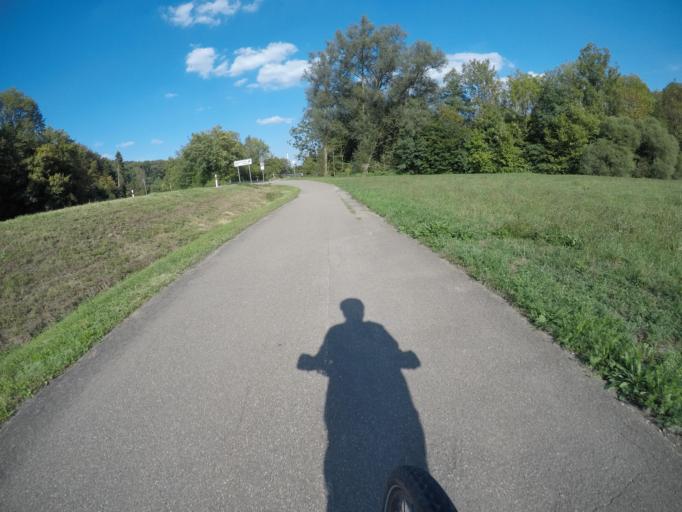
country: DE
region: Baden-Wuerttemberg
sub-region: Regierungsbezirk Stuttgart
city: Denkendorf
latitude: 48.6997
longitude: 9.3398
